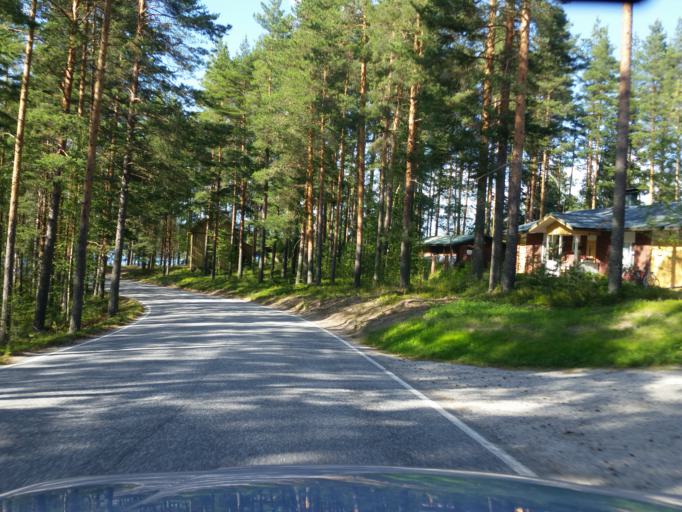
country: FI
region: Southern Savonia
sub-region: Savonlinna
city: Sulkava
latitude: 61.7723
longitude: 28.4337
